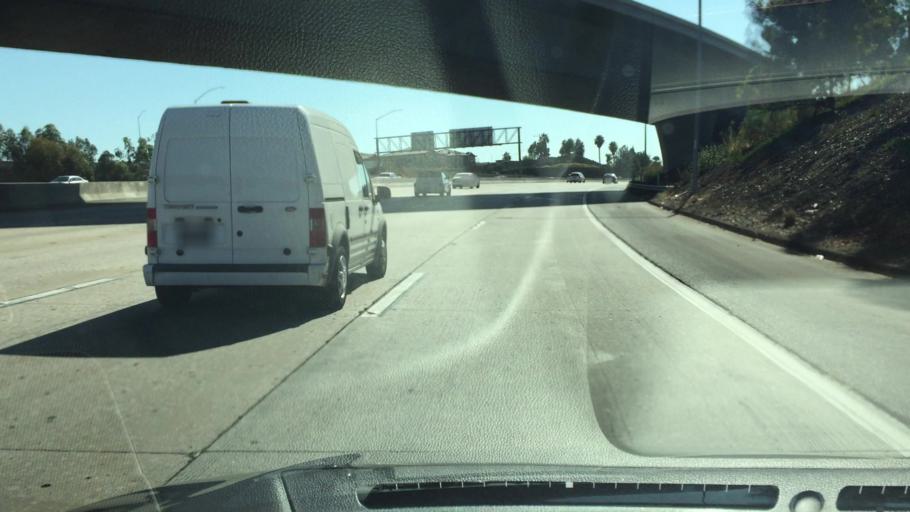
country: US
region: California
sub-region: San Diego County
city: Lemon Grove
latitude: 32.7474
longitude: -117.0198
